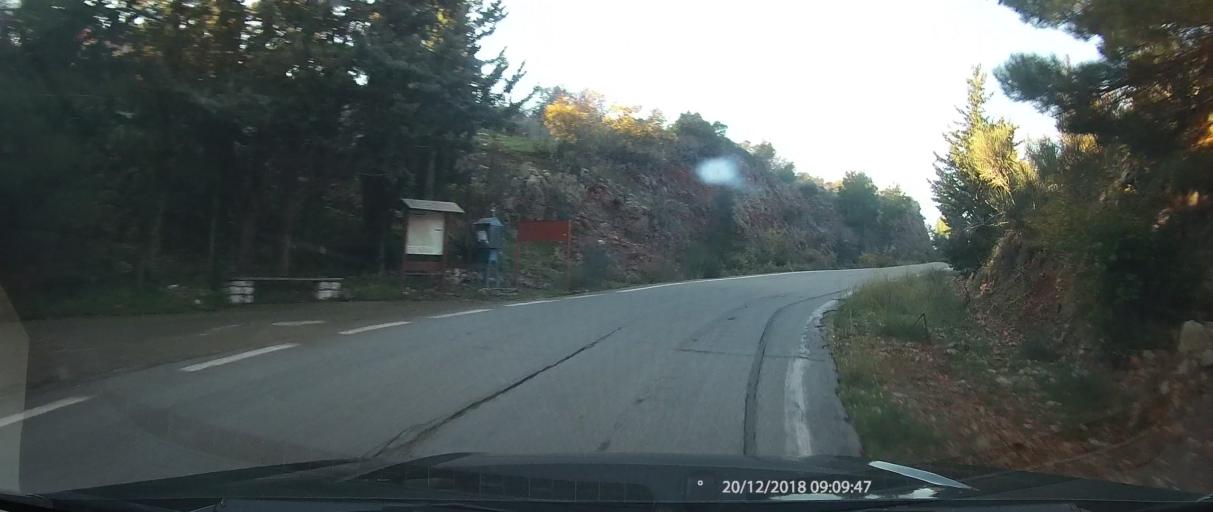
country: GR
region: Peloponnese
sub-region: Nomos Lakonias
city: Sykea
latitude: 36.9145
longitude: 23.0028
